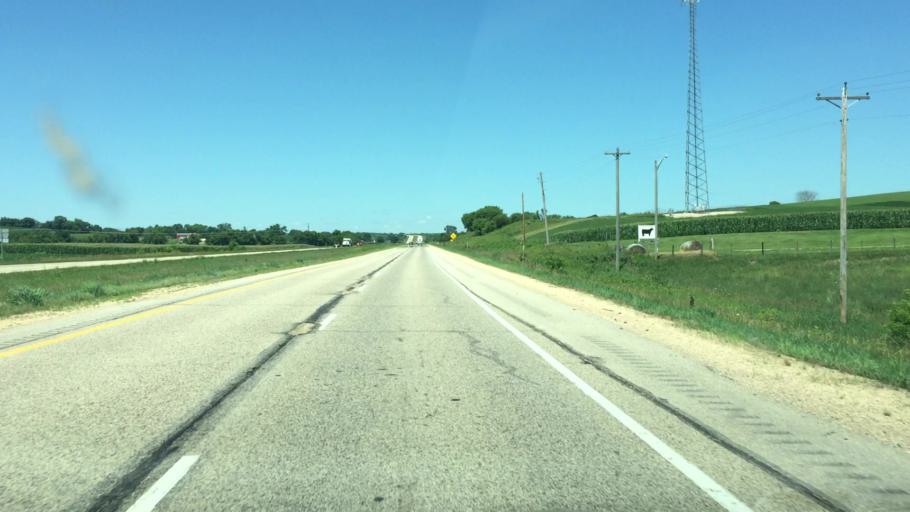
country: US
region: Iowa
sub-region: Jackson County
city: Maquoketa
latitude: 42.1651
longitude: -90.6756
